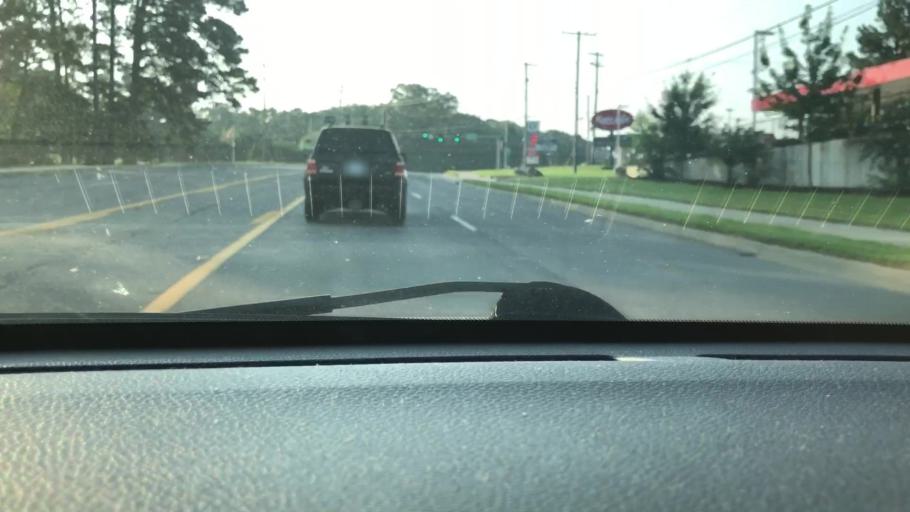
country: US
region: Arkansas
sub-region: Saline County
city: Bryant
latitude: 34.6107
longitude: -92.4944
